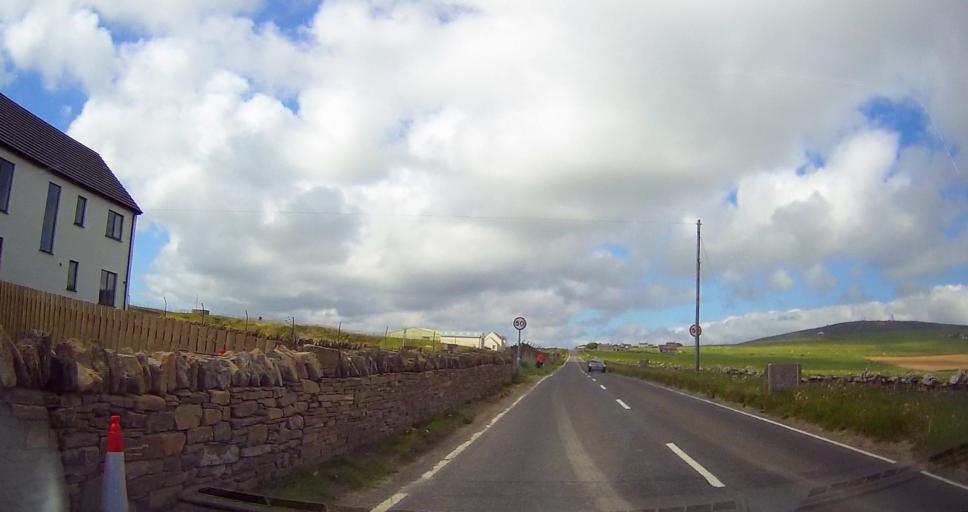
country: GB
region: Scotland
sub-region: Orkney Islands
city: Orkney
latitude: 58.9775
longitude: -2.9863
